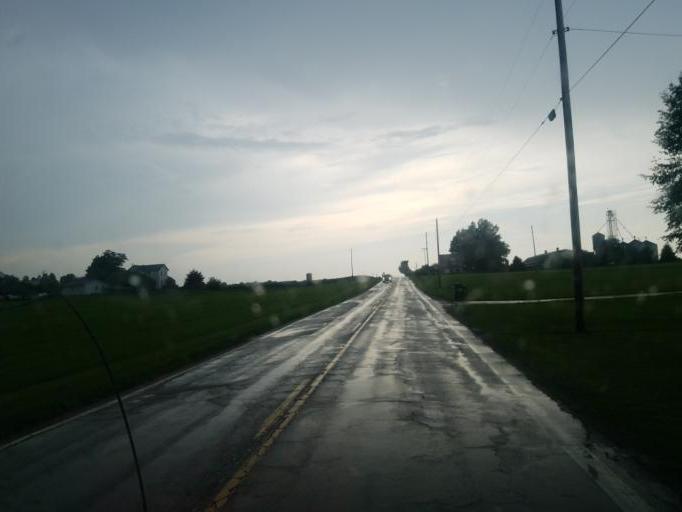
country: US
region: Ohio
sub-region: Wayne County
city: Creston
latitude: 40.9458
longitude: -81.8697
